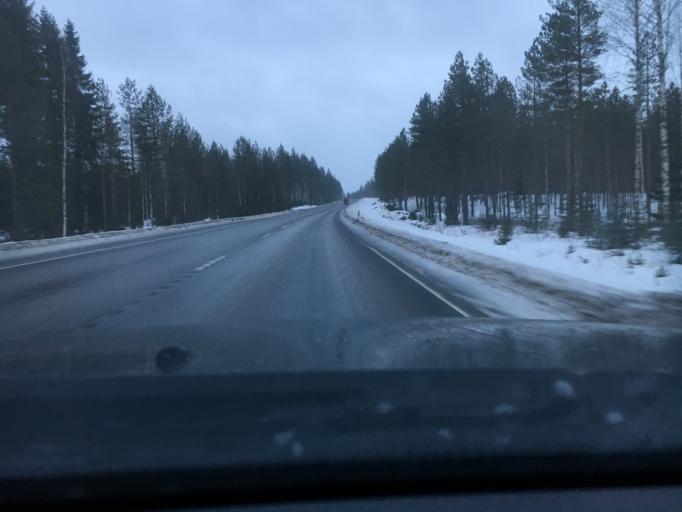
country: FI
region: Central Finland
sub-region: Jyvaeskylae
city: Hankasalmi
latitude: 62.3904
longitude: 26.6209
